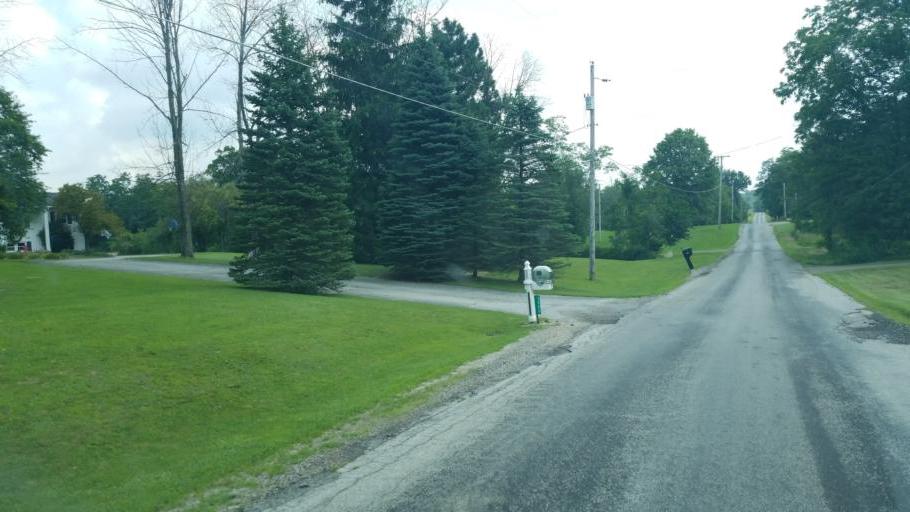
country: US
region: Ohio
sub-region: Richland County
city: Ontario
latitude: 40.8013
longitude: -82.6262
